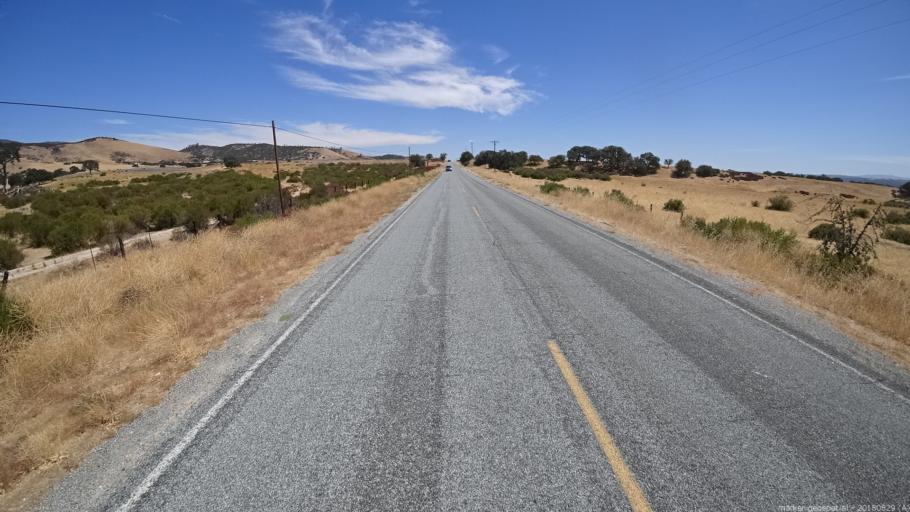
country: US
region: California
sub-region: San Luis Obispo County
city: Lake Nacimiento
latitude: 35.9297
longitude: -121.0510
